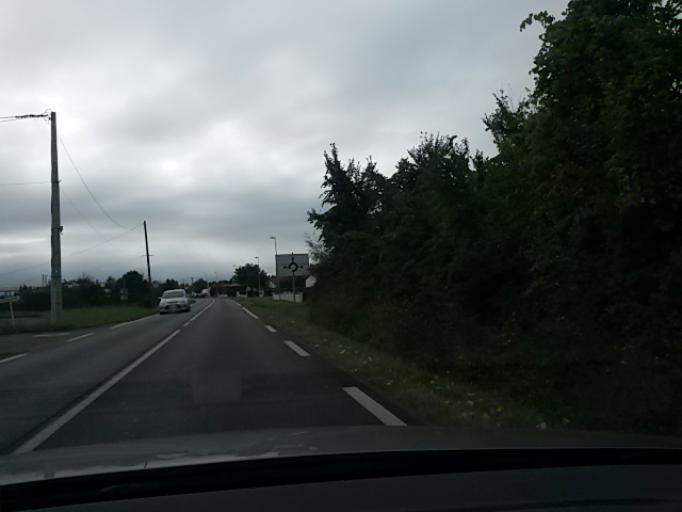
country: FR
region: Poitou-Charentes
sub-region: Departement de la Charente-Maritime
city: Saint-Trojan-les-Bains
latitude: 45.8799
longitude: -1.2211
